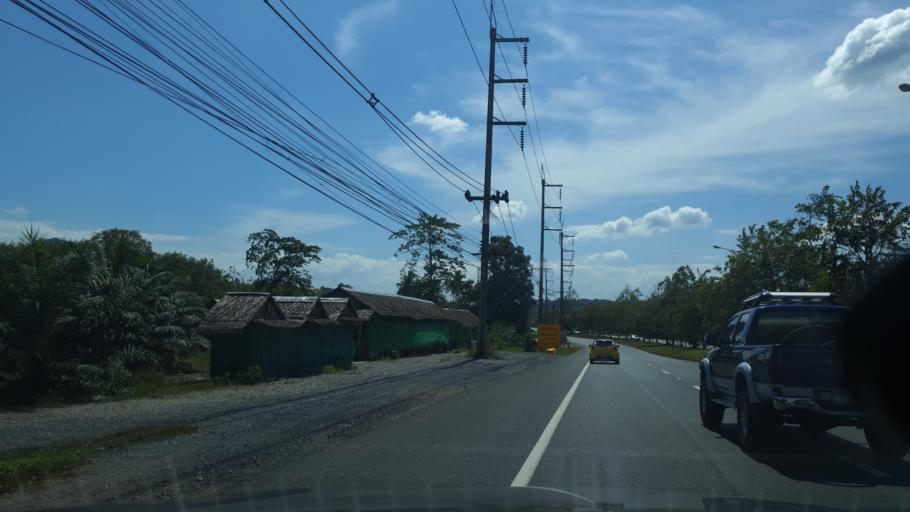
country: TH
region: Phangnga
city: Takua Thung
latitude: 8.2893
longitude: 98.3732
